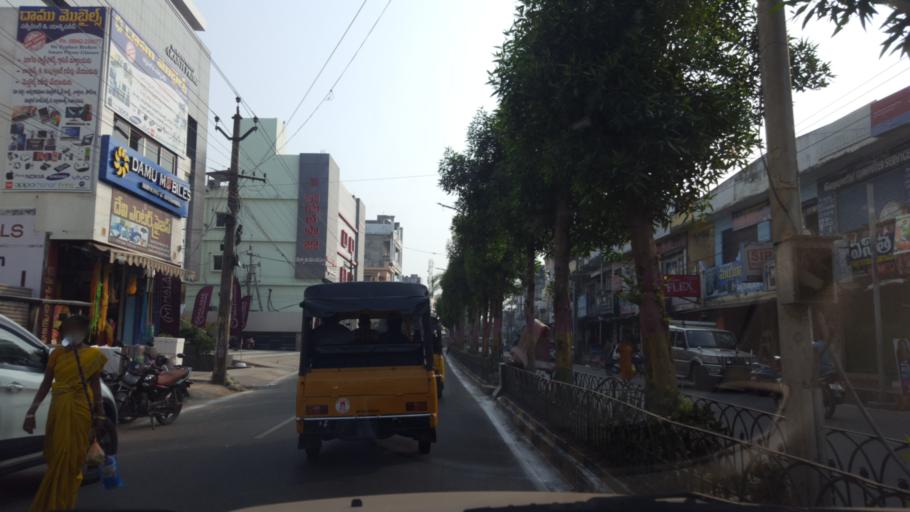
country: IN
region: Andhra Pradesh
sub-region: Srikakulam
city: Srikakulam
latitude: 18.2985
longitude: 83.8948
